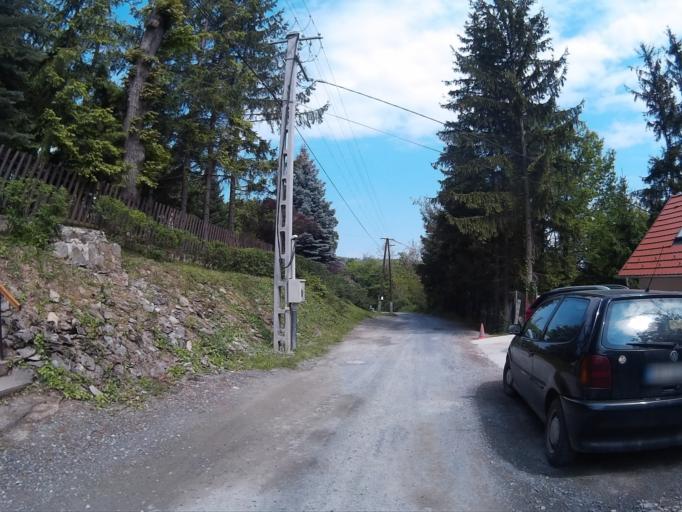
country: HU
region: Vas
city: Koszeg
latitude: 47.3780
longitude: 16.5207
